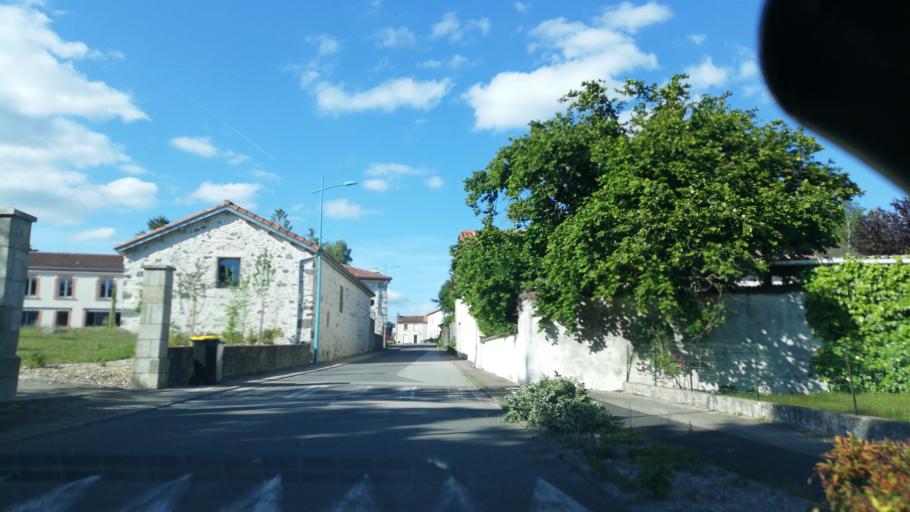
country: FR
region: Poitou-Charentes
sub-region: Departement des Deux-Sevres
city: Moncoutant
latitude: 46.7178
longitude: -0.5874
